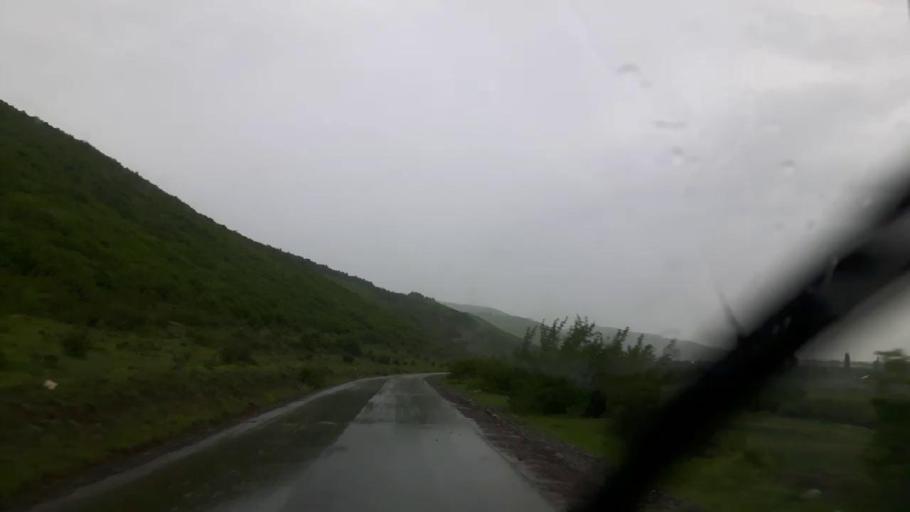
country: GE
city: Agara
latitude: 41.9831
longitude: 43.9294
